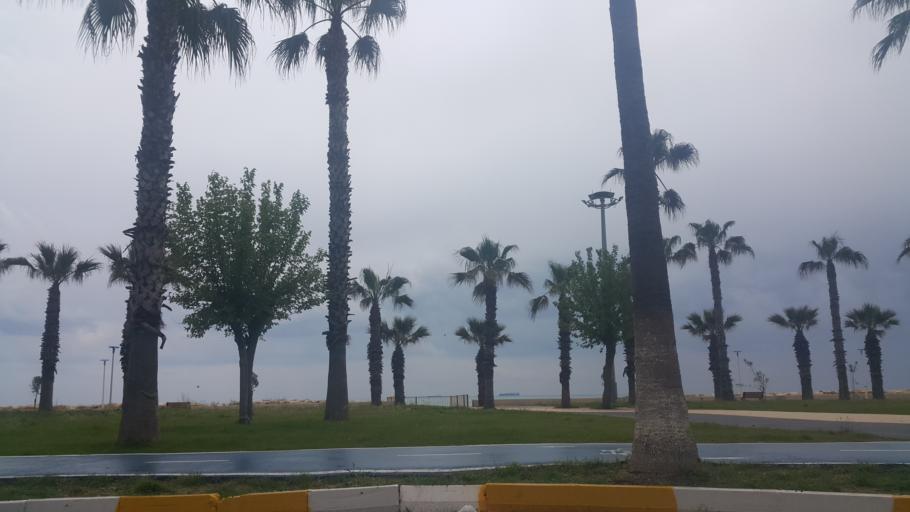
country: TR
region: Mersin
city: Mercin
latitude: 36.7783
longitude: 34.5878
